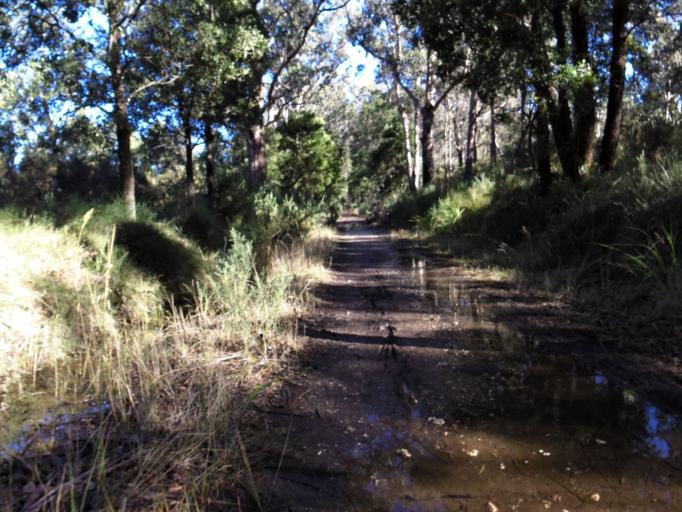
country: AU
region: Victoria
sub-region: Moorabool
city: Bacchus Marsh
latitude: -37.3888
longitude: 144.3002
